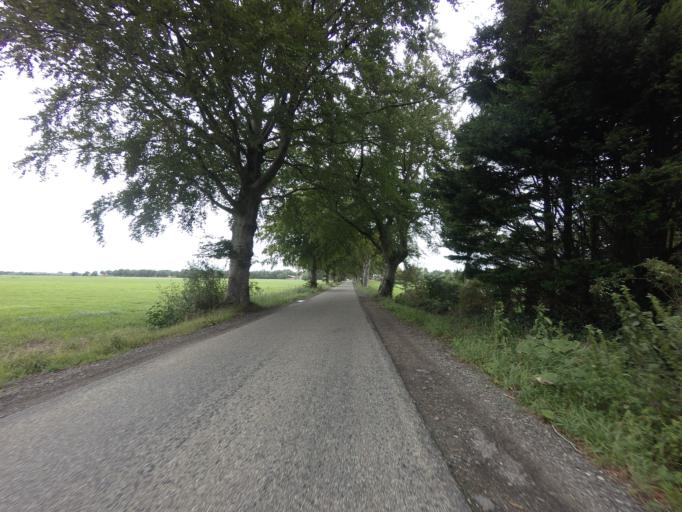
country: NL
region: Friesland
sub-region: Gemeente Weststellingwerf
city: Steggerda
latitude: 52.8771
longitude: 6.0923
